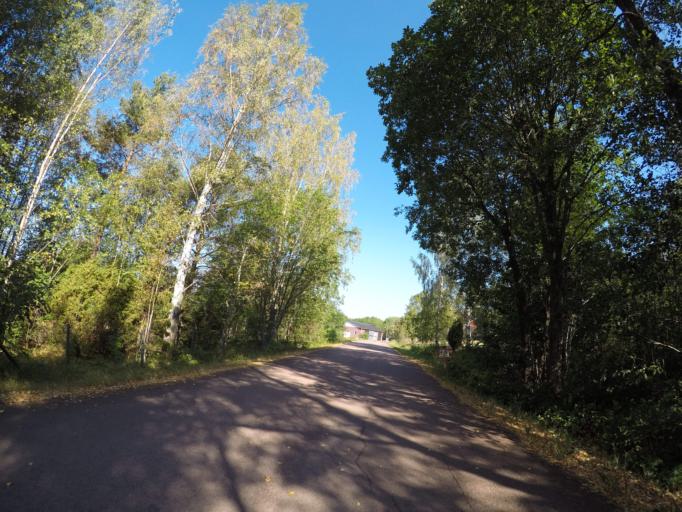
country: AX
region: Alands landsbygd
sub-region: Finstroem
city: Finstroem
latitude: 60.3297
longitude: 19.9122
